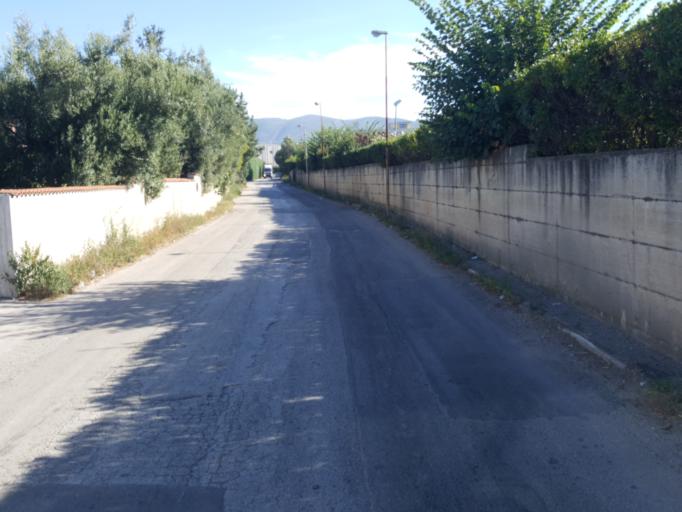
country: IT
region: Campania
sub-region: Provincia di Caserta
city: Pignataro Maggiore
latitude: 41.1618
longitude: 14.1627
